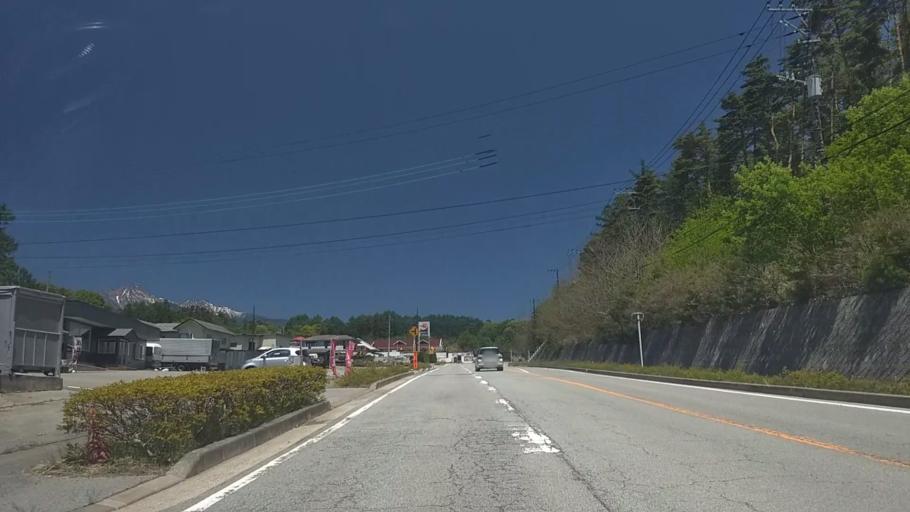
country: JP
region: Yamanashi
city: Nirasaki
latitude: 35.8872
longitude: 138.4394
